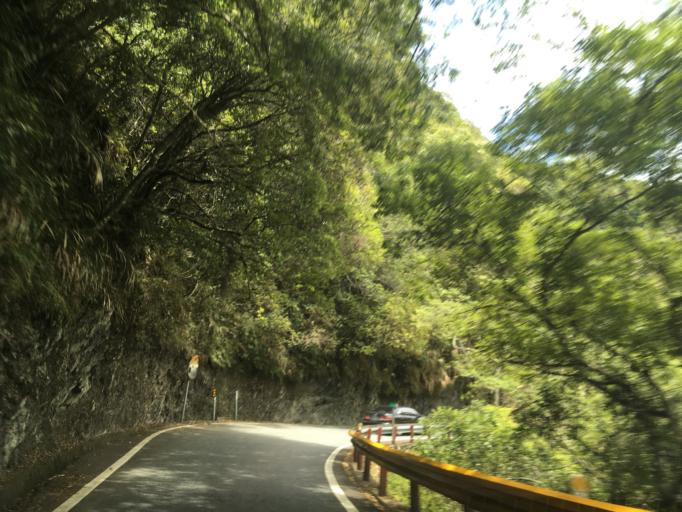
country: TW
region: Taiwan
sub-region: Hualien
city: Hualian
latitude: 24.1929
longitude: 121.4789
